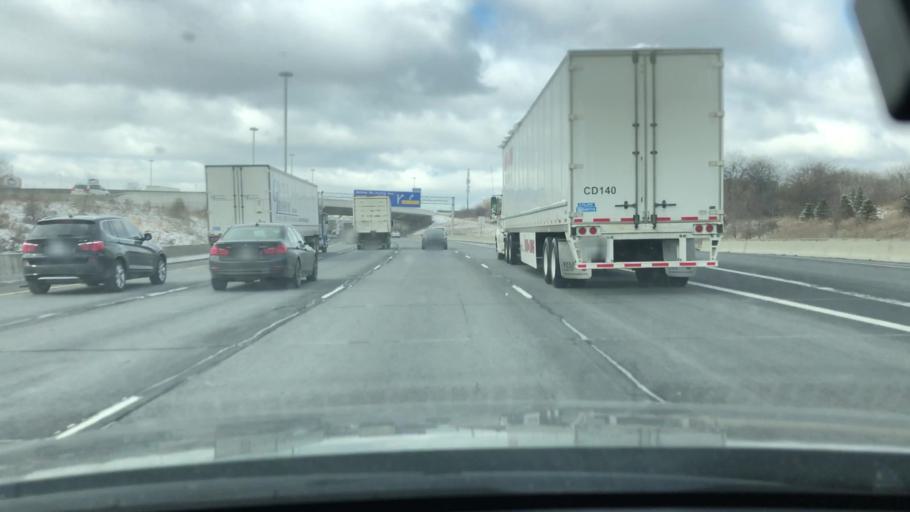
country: CA
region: Ontario
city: Etobicoke
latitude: 43.7131
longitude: -79.5448
